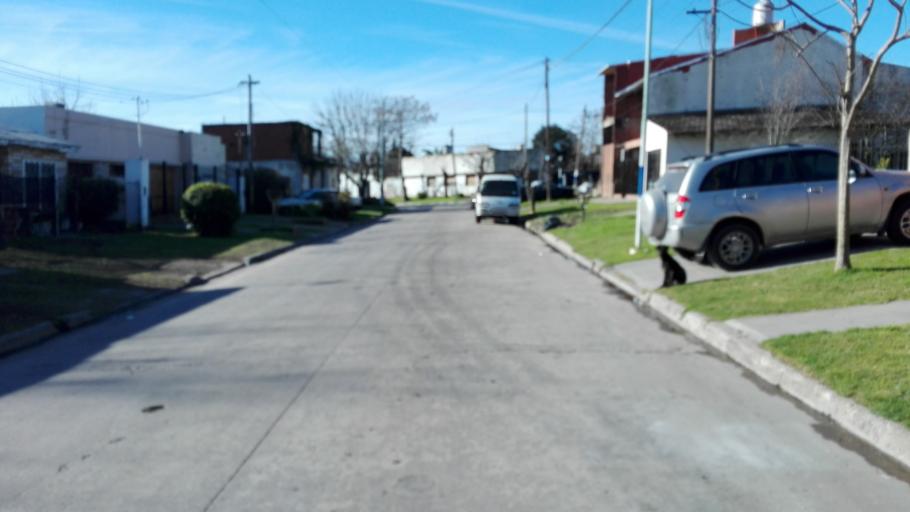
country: AR
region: Buenos Aires
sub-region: Partido de La Plata
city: La Plata
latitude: -34.8806
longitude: -57.9901
